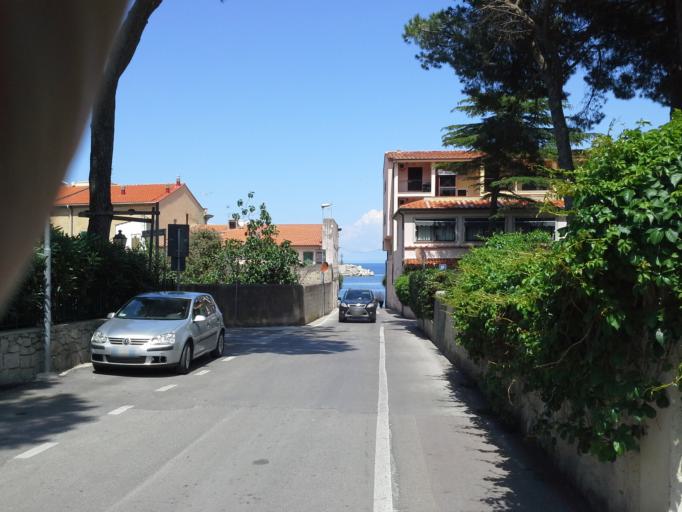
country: IT
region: Tuscany
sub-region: Provincia di Livorno
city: Marciana Marina
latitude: 42.8060
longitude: 10.1961
